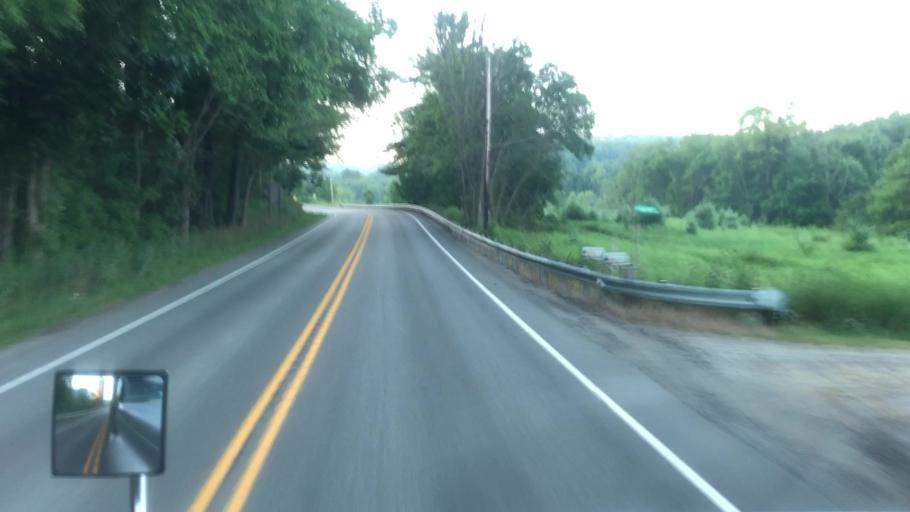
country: US
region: Pennsylvania
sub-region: Crawford County
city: Titusville
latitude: 41.6185
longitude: -79.6384
